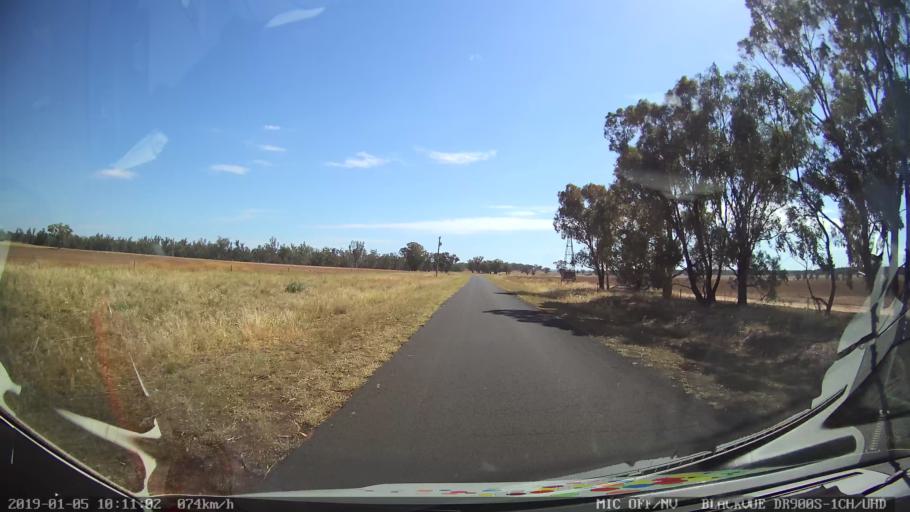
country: AU
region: New South Wales
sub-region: Gilgandra
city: Gilgandra
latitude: -31.6164
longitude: 148.8974
